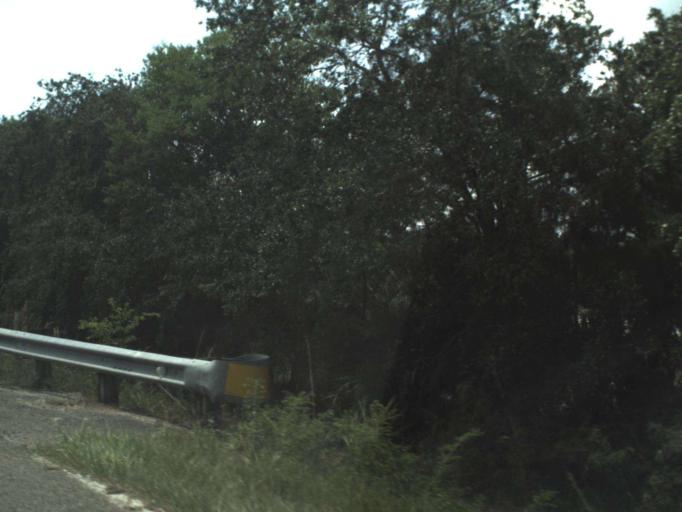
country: US
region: Florida
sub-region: Volusia County
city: Oak Hill
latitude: 28.8280
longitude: -80.8515
